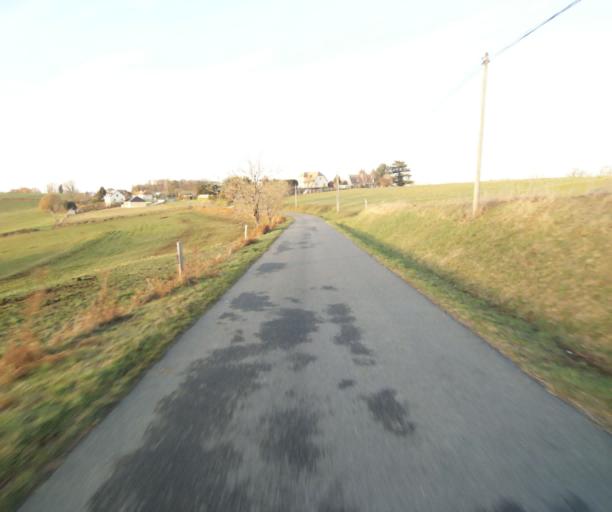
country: FR
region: Limousin
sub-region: Departement de la Correze
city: Laguenne
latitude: 45.2263
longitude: 1.8264
